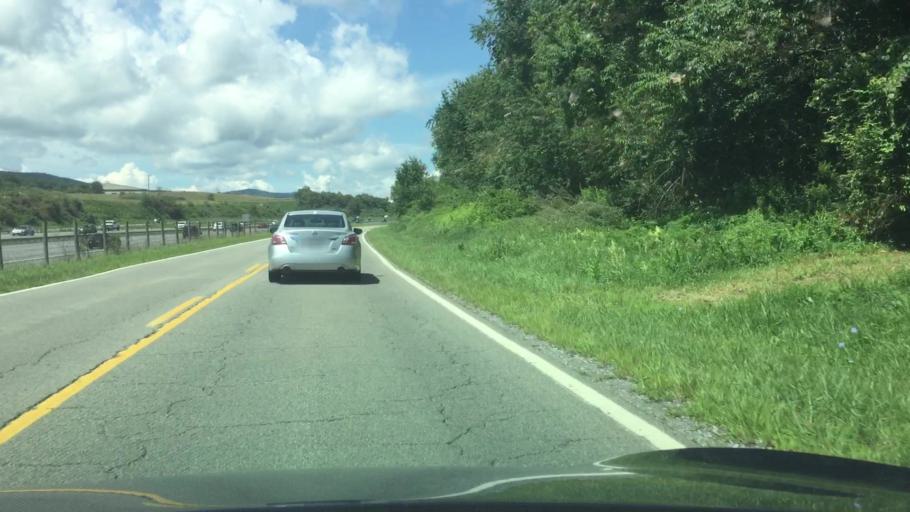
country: US
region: Virginia
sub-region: Wythe County
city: Wytheville
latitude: 36.9388
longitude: -80.9817
